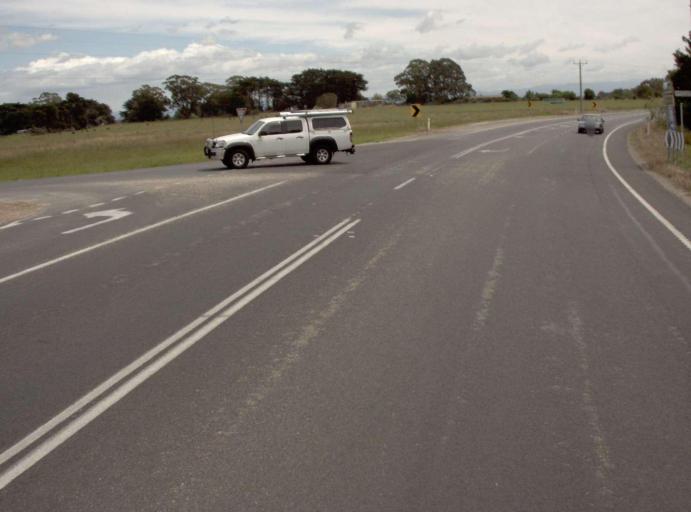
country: AU
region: Victoria
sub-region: Wellington
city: Sale
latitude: -38.0649
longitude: 147.0297
